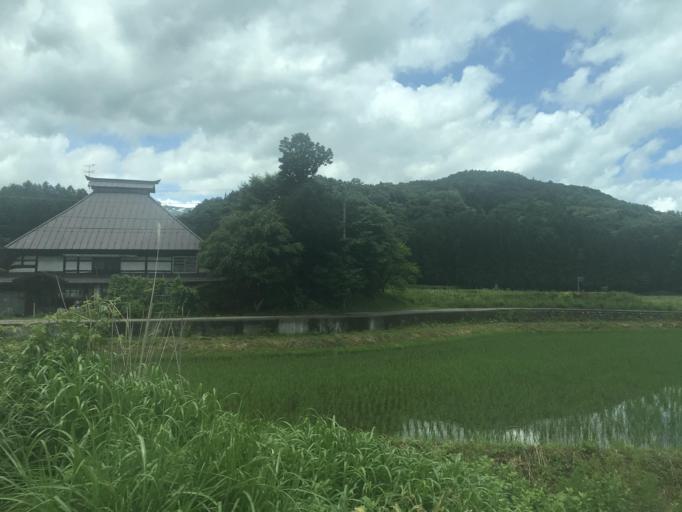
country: JP
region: Nagano
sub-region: Kitaazumi Gun
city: Hakuba
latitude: 36.7131
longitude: 137.8781
